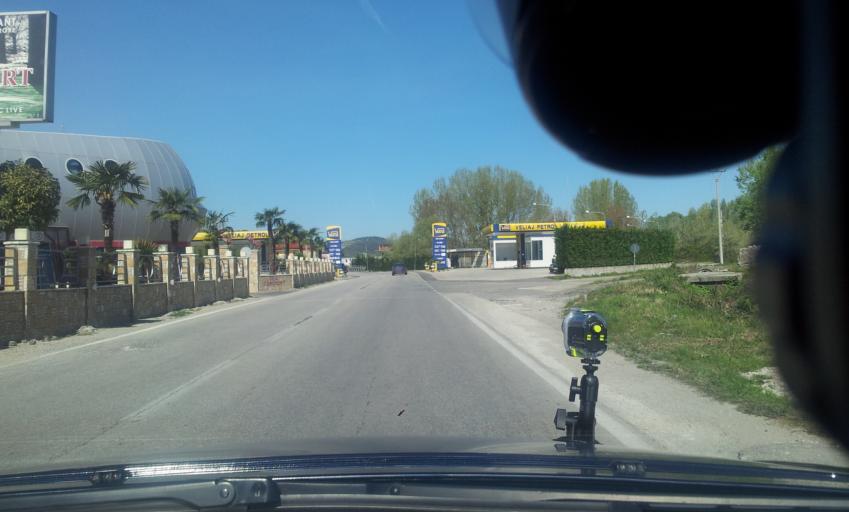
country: AL
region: Tirane
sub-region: Rrethi i Tiranes
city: Preze
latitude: 41.4349
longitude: 19.6987
